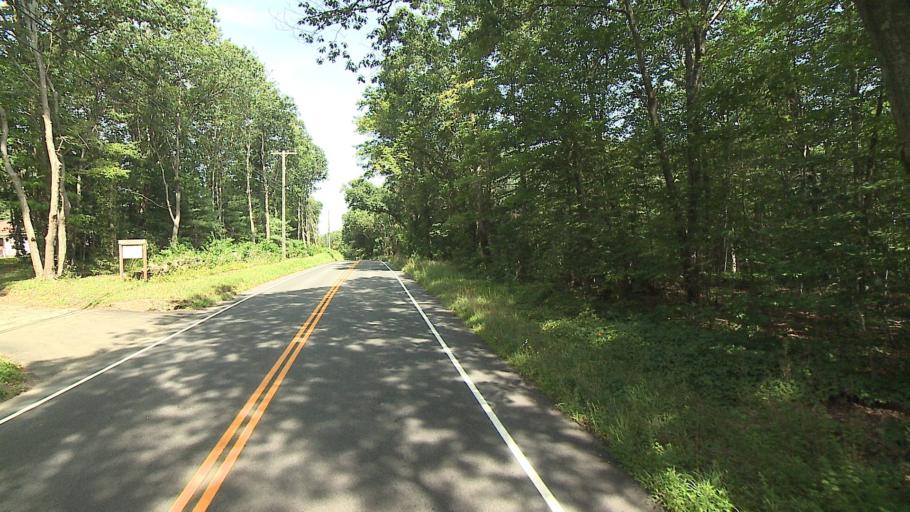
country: US
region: Connecticut
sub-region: Litchfield County
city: Bethlehem Village
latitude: 41.6187
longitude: -73.1982
